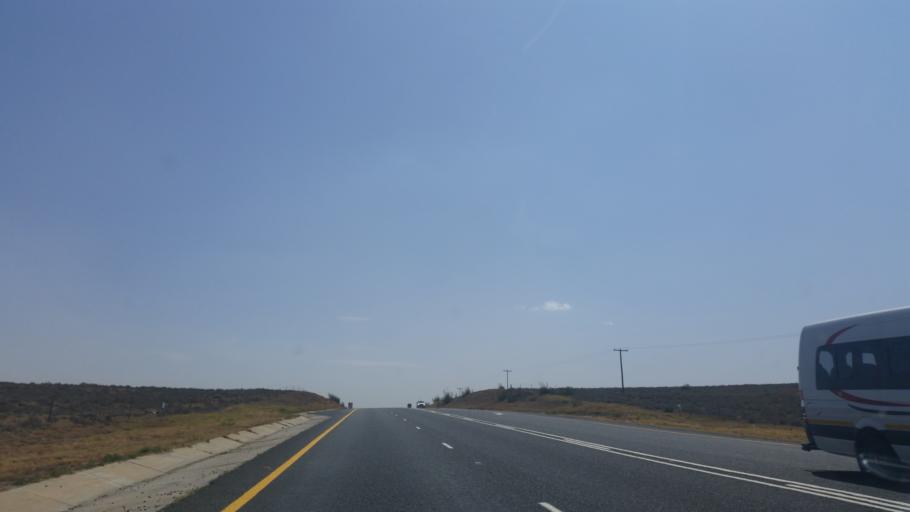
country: ZA
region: Orange Free State
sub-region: Thabo Mofutsanyana District Municipality
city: Bethlehem
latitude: -28.3044
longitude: 28.5697
